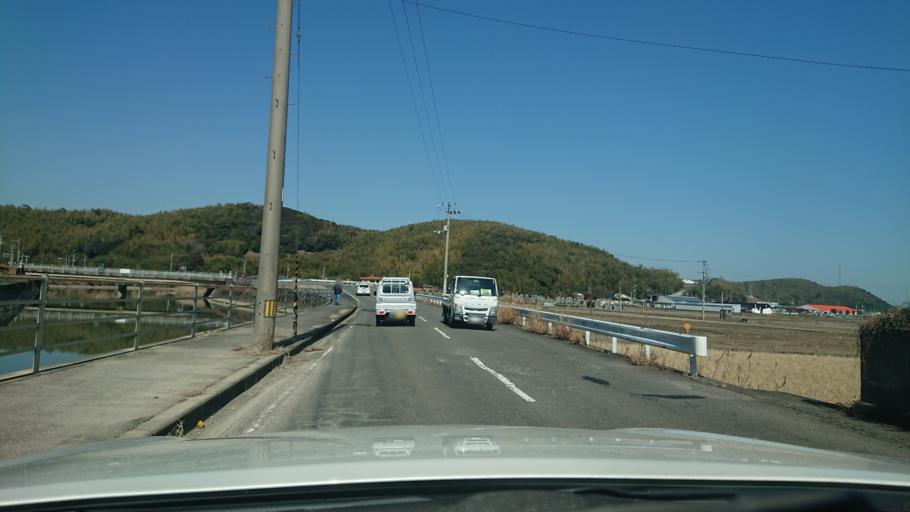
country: JP
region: Tokushima
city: Komatsushimacho
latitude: 33.9688
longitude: 134.6020
